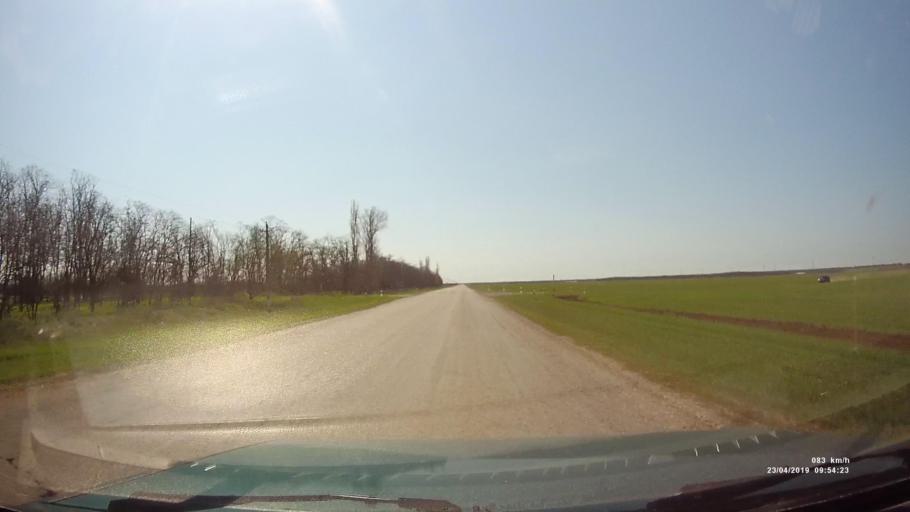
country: RU
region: Rostov
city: Orlovskiy
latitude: 46.8216
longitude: 42.0549
